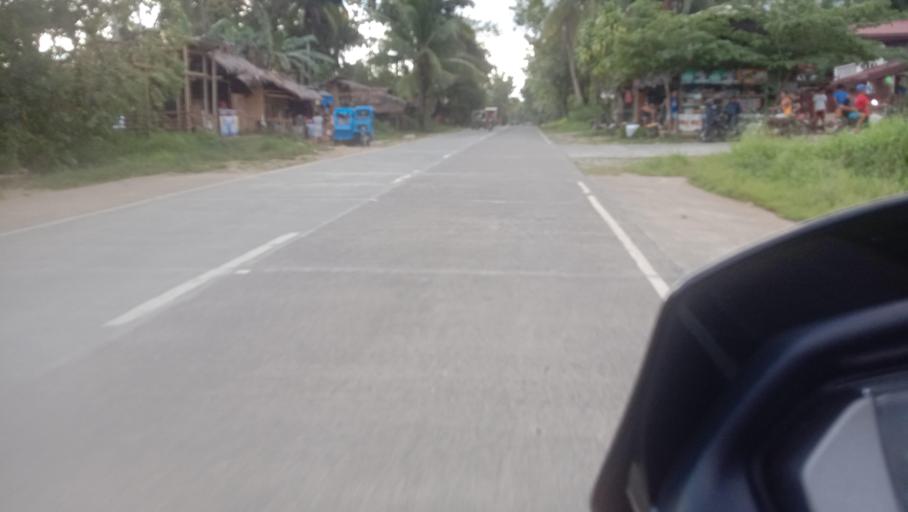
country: PH
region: Caraga
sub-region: Province of Surigao del Sur
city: Barobo
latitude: 8.5154
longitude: 126.1249
